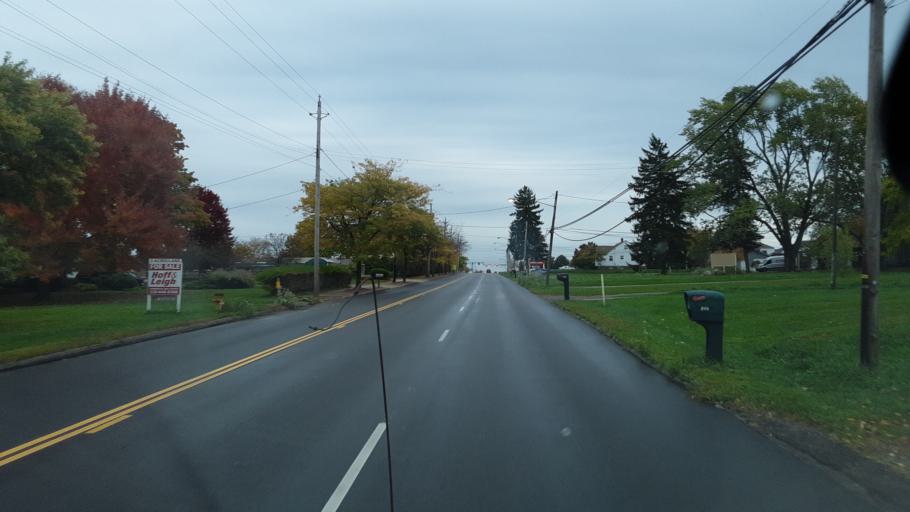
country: US
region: Ohio
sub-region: Summit County
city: Portage Lakes
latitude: 41.0296
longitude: -81.4967
